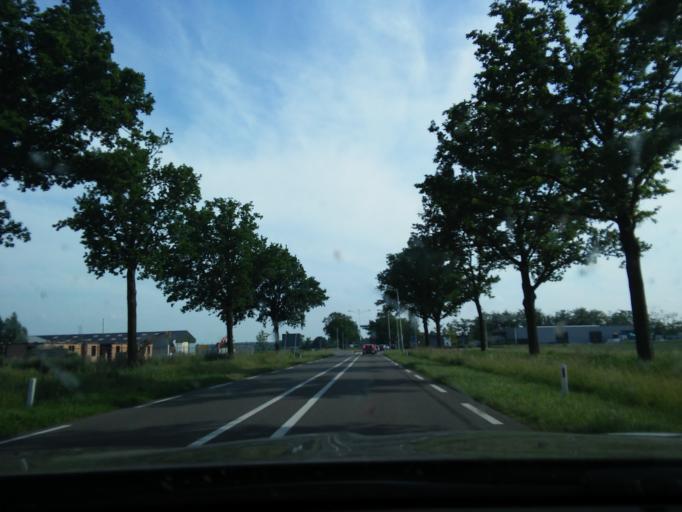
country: BE
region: Flanders
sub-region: Provincie Oost-Vlaanderen
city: Maldegem
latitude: 51.2581
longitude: 3.4524
